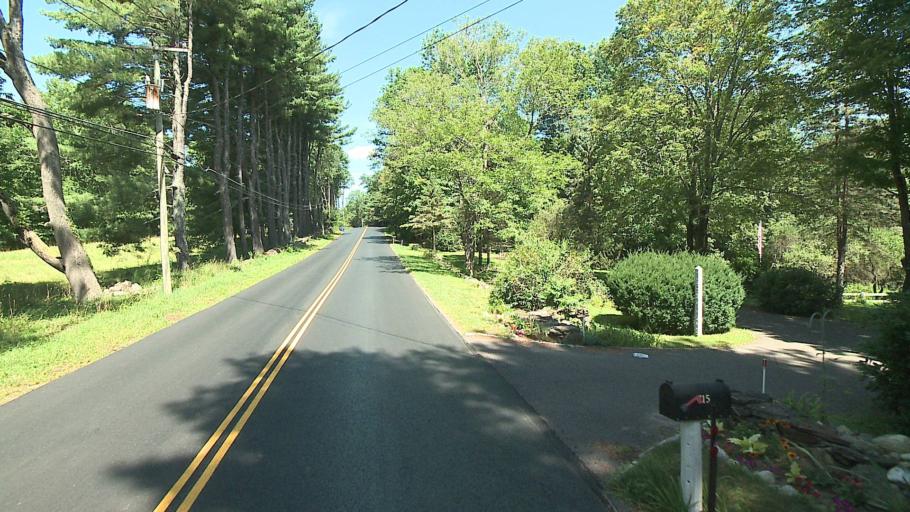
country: US
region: Connecticut
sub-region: Hartford County
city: West Simsbury
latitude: 41.9142
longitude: -72.9017
